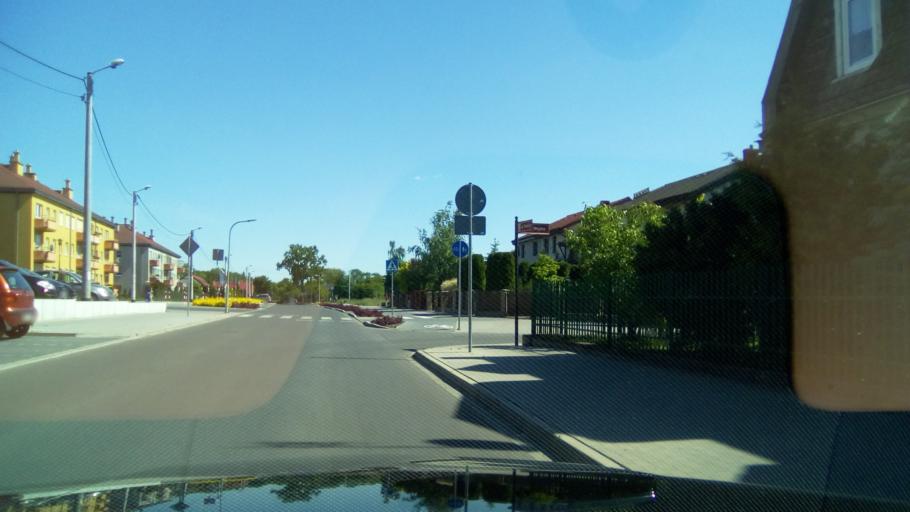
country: PL
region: Greater Poland Voivodeship
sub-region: Powiat gnieznienski
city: Gniezno
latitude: 52.5220
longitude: 17.6121
